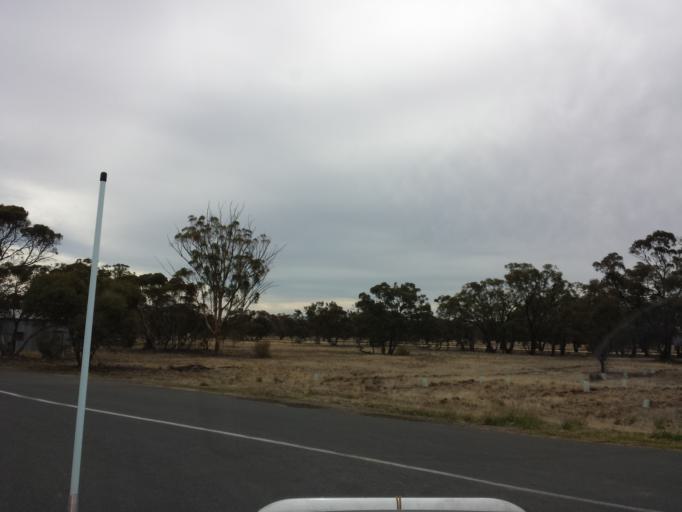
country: AU
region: Victoria
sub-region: Horsham
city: Horsham
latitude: -36.0762
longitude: 142.4210
